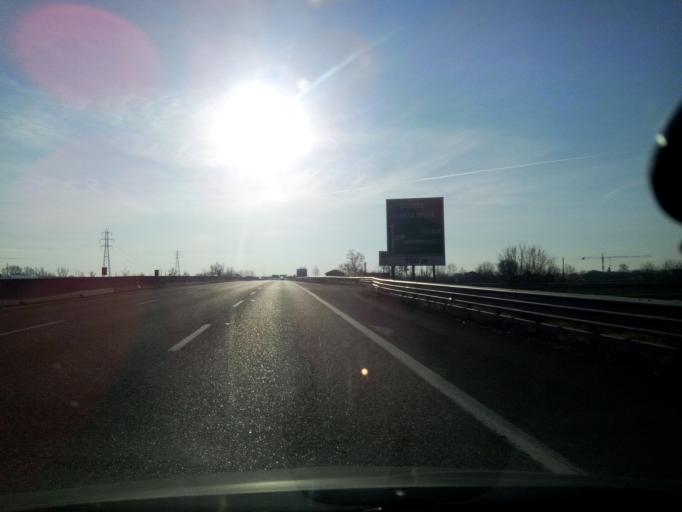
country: IT
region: Emilia-Romagna
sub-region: Provincia di Parma
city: Fidenza
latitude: 44.8906
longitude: 10.0801
